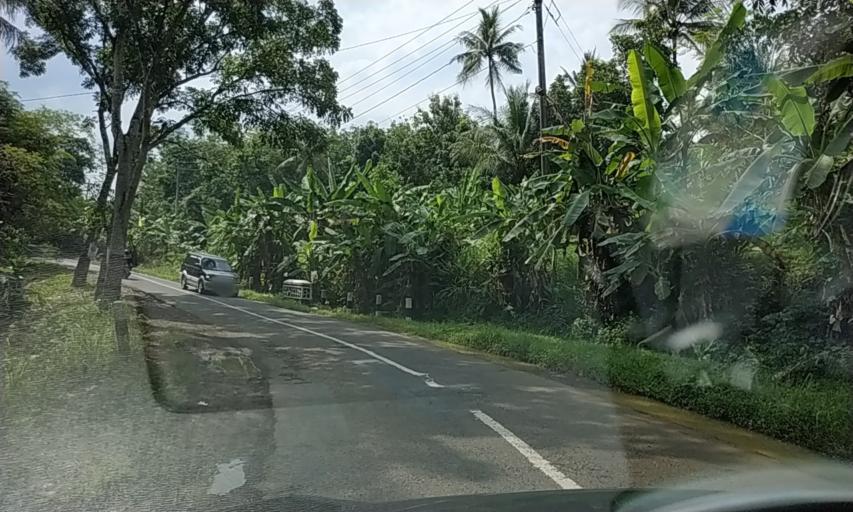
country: ID
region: Central Java
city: Winangun
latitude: -7.3692
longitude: 108.6995
